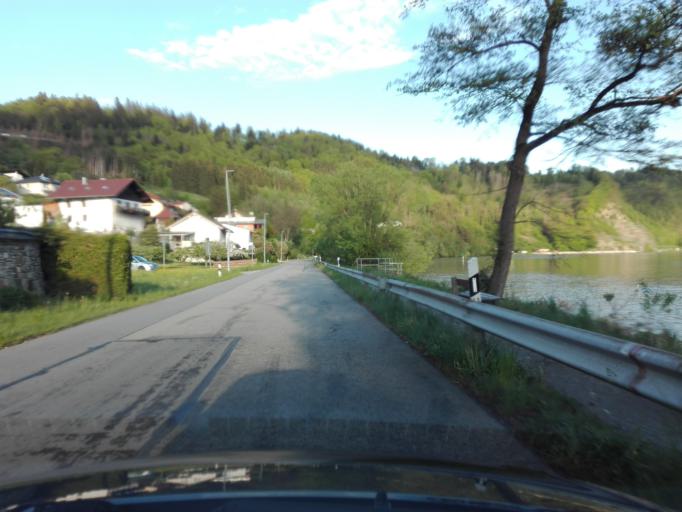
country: DE
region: Bavaria
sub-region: Lower Bavaria
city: Obernzell
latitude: 48.5526
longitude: 13.6473
